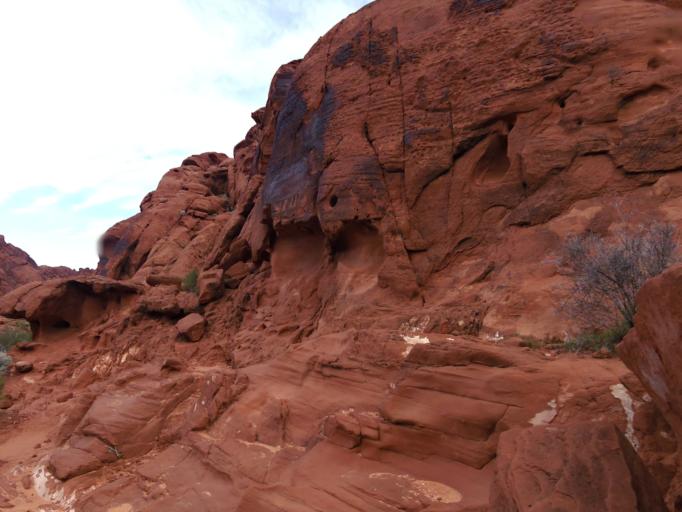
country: US
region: Nevada
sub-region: Clark County
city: Moapa Valley
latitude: 36.4399
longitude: -114.5149
